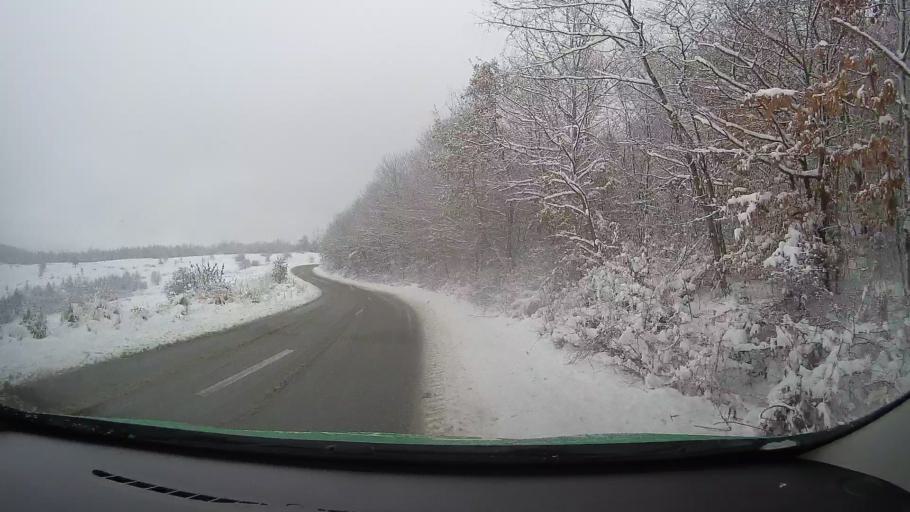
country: RO
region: Hunedoara
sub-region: Comuna Teliucu Inferior
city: Teliucu Inferior
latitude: 45.6841
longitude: 22.9100
